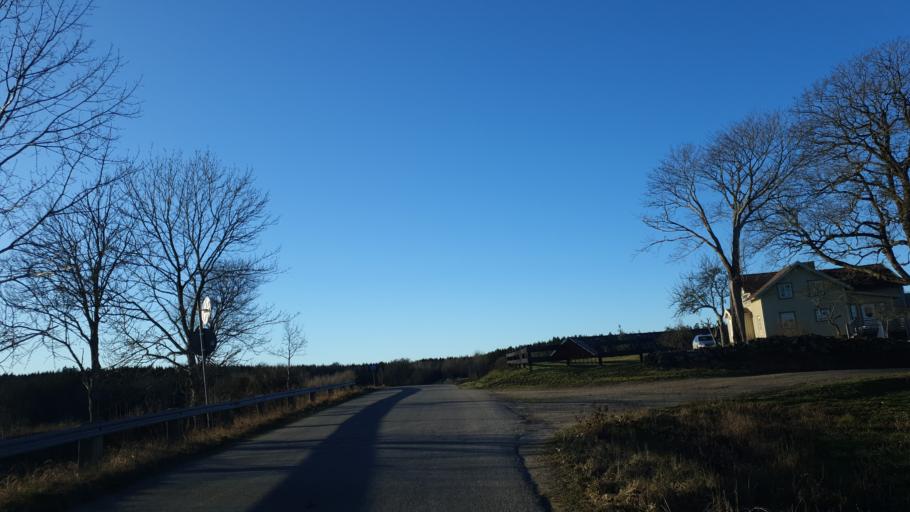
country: SE
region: Blekinge
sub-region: Karlskrona Kommun
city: Nattraby
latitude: 56.2642
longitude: 15.5033
